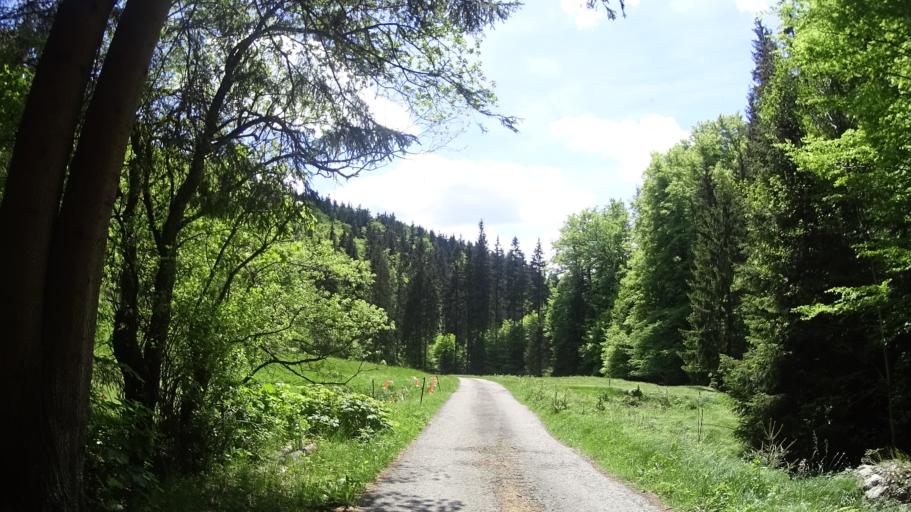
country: DE
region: Thuringia
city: Neustadt am Rennsteig
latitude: 50.5702
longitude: 10.9162
